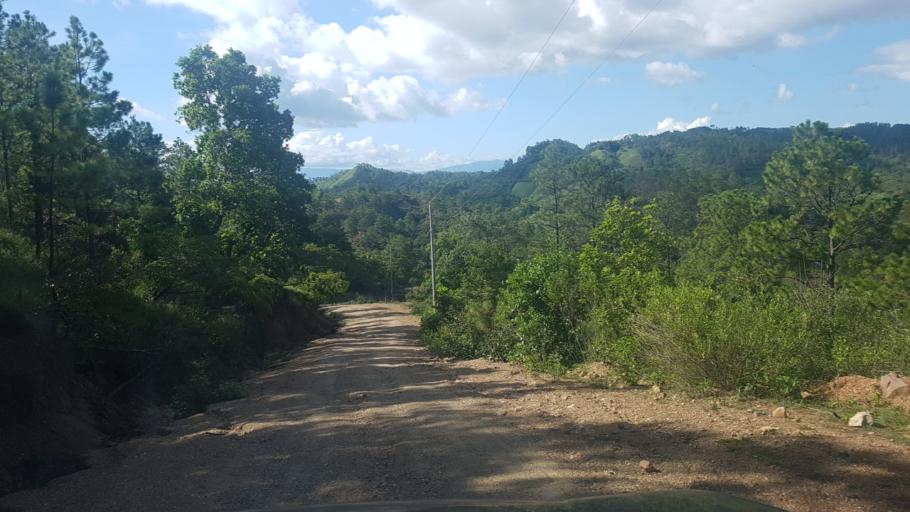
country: HN
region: Choluteca
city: Duyure
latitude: 13.6464
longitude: -86.6538
